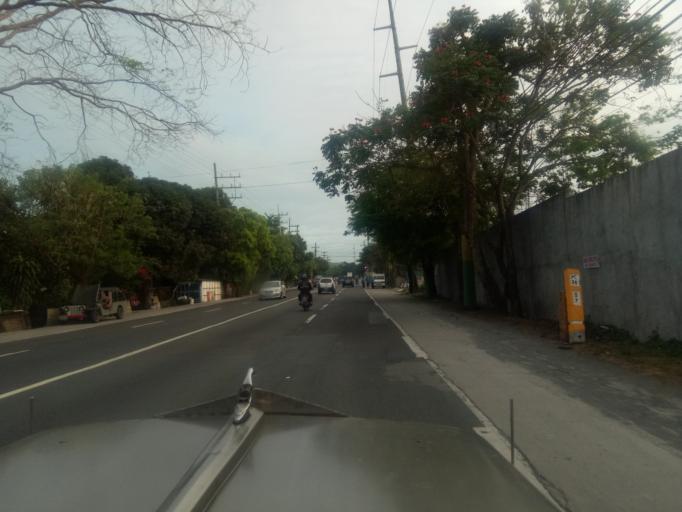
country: PH
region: Calabarzon
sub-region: Province of Cavite
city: Biga
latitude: 14.2875
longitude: 120.9593
